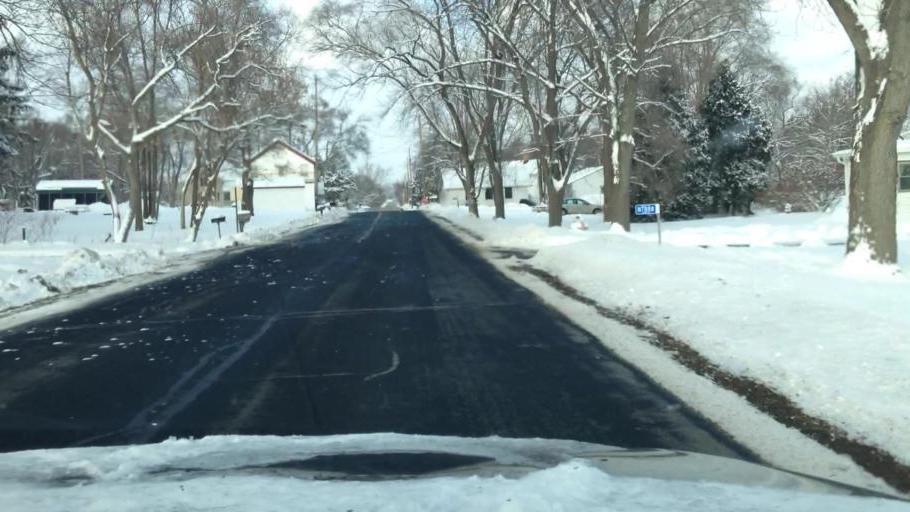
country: US
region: Wisconsin
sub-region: Walworth County
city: East Troy
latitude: 42.7774
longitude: -88.4451
